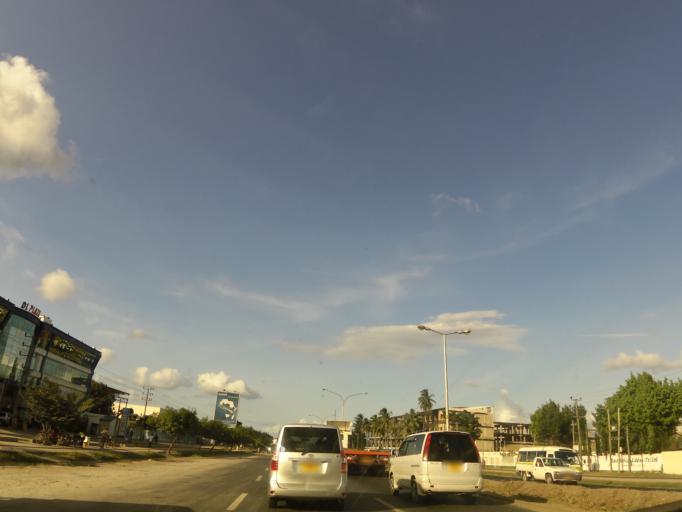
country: TZ
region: Dar es Salaam
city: Dar es Salaam
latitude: -6.8514
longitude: 39.2306
